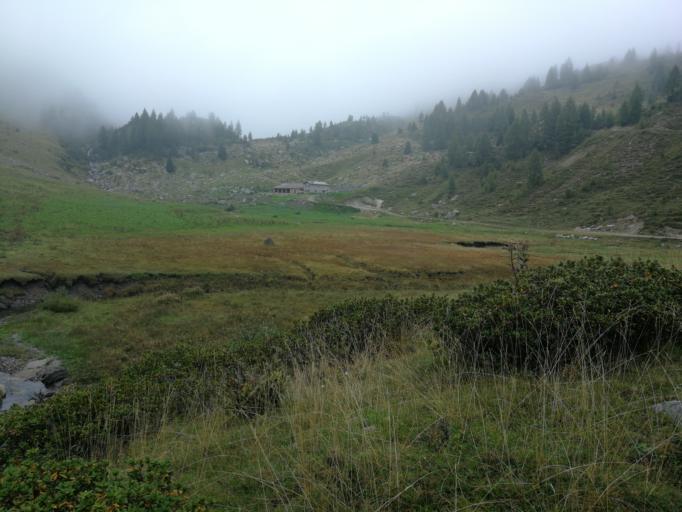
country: IT
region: Trentino-Alto Adige
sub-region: Provincia di Trento
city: Brione
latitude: 45.9241
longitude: 10.5203
